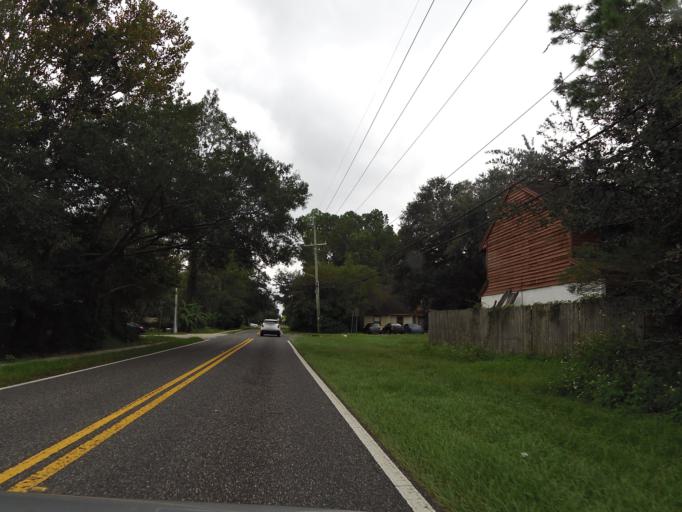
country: US
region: Florida
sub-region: Clay County
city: Bellair-Meadowbrook Terrace
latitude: 30.2575
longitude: -81.7732
